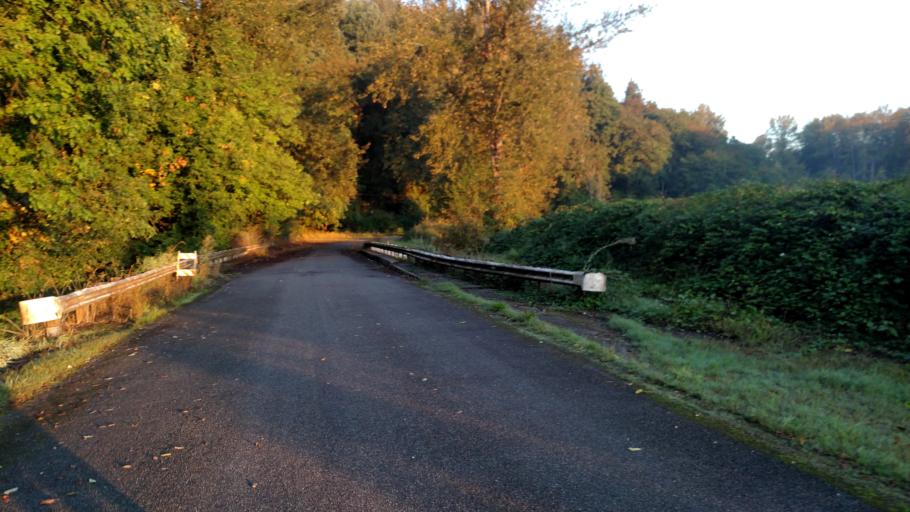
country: US
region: Washington
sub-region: King County
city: Kent
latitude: 47.3919
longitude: -122.2735
